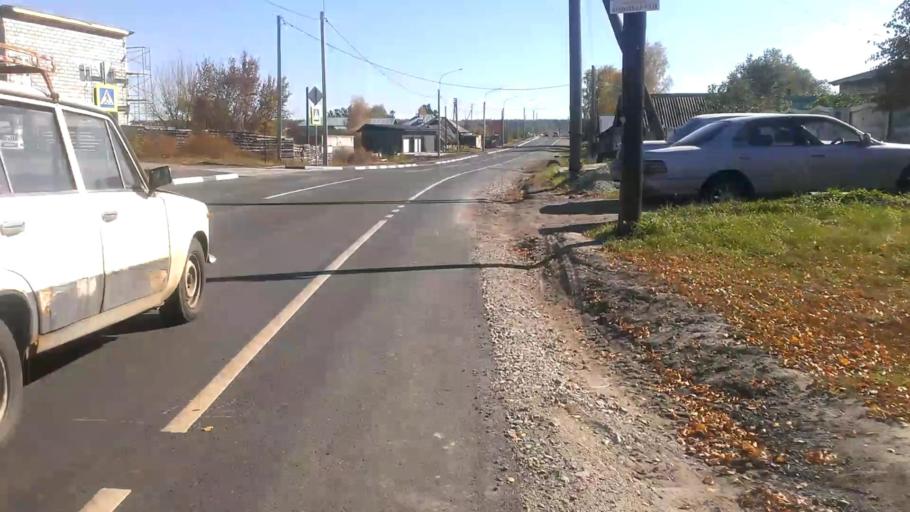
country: RU
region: Altai Krai
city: Sannikovo
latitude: 53.3163
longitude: 83.9580
